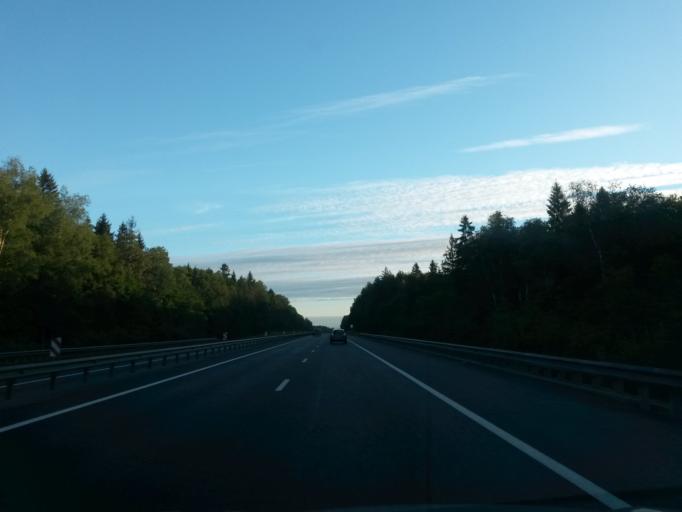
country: RU
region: Moskovskaya
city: Svatkovo
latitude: 56.3989
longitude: 38.3273
